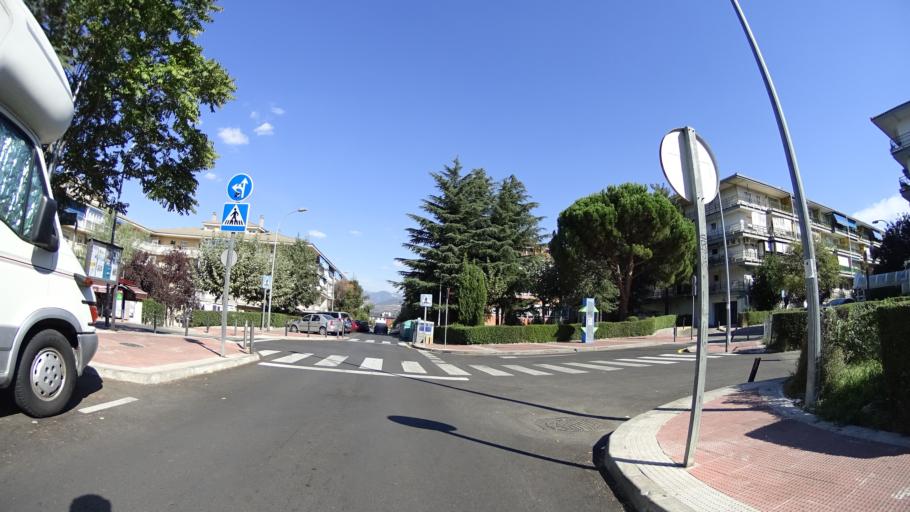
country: ES
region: Madrid
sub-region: Provincia de Madrid
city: Collado-Villalba
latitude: 40.6215
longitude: -4.0114
